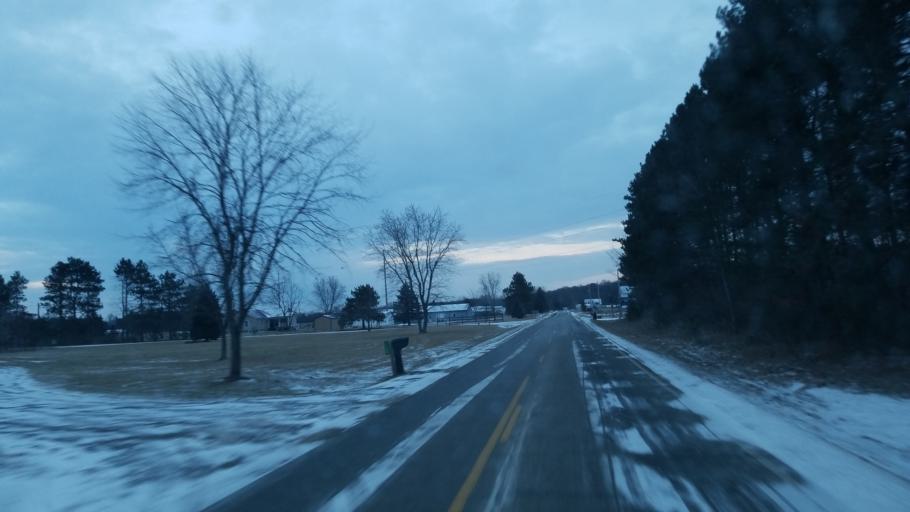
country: US
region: Michigan
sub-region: Osceola County
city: Reed City
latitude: 43.8302
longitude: -85.4241
